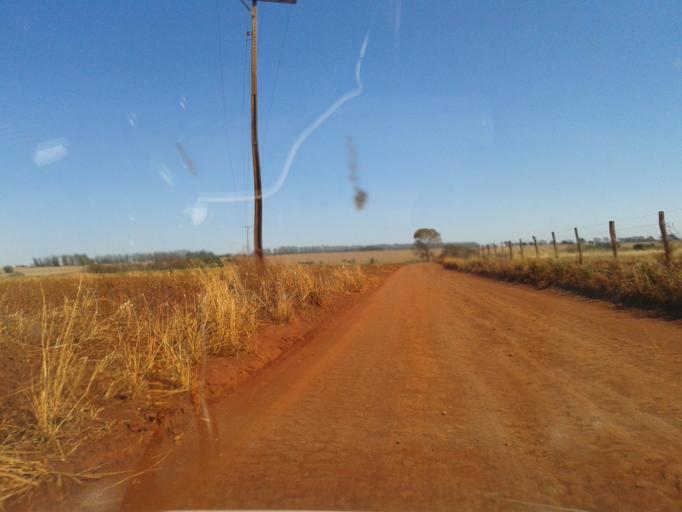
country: BR
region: Minas Gerais
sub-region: Centralina
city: Centralina
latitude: -18.5915
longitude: -49.1715
